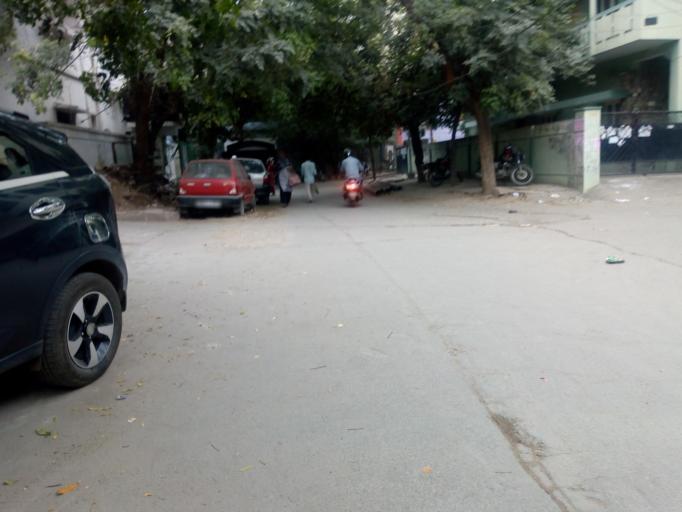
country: IN
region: Telangana
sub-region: Hyderabad
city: Hyderabad
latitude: 17.4346
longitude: 78.4426
